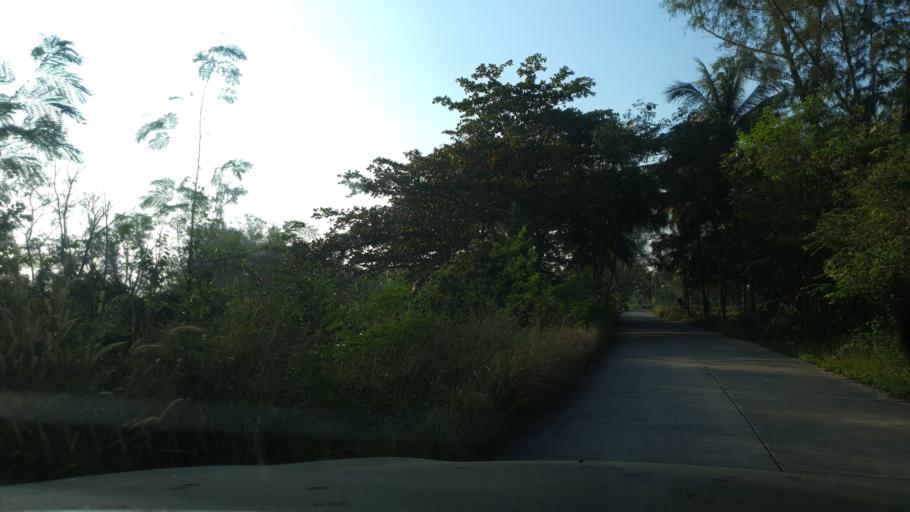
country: TH
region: Prachuap Khiri Khan
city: Bang Saphan
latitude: 11.2860
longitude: 99.5490
